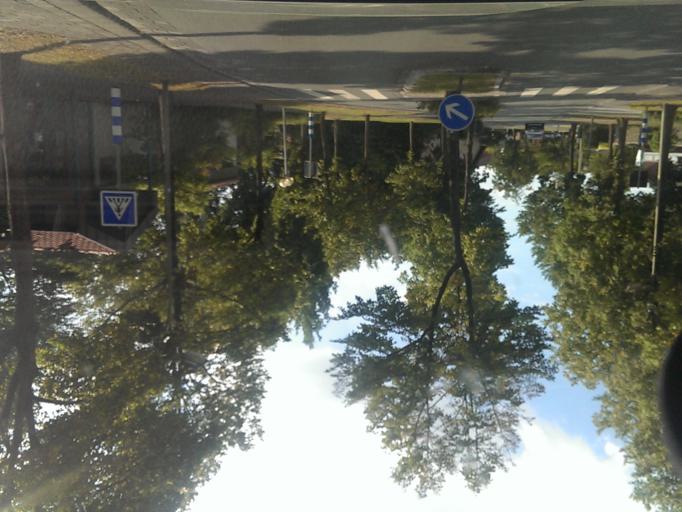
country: DE
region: North Rhine-Westphalia
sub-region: Regierungsbezirk Detmold
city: Delbruck
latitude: 51.7446
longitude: 8.5109
